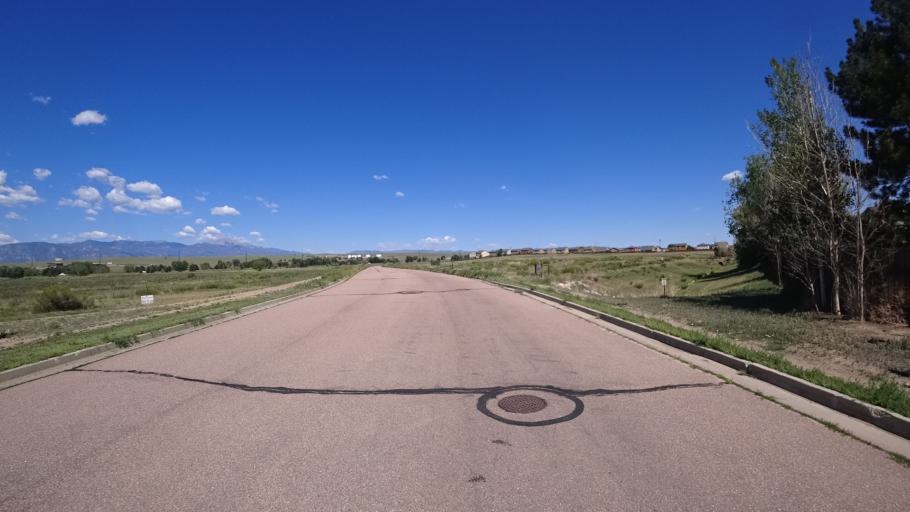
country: US
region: Colorado
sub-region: El Paso County
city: Security-Widefield
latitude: 38.7716
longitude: -104.6532
